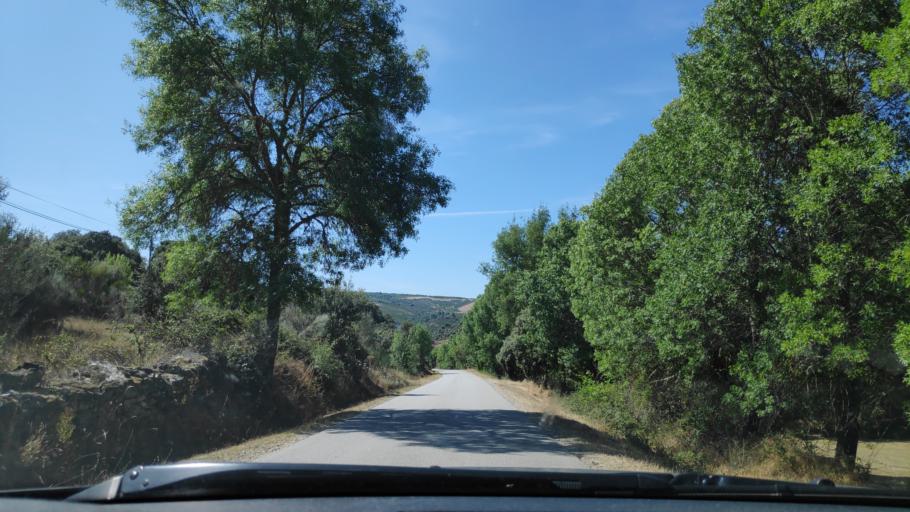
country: ES
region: Castille and Leon
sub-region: Provincia de Zamora
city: Trabazos
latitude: 41.7431
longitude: -6.5777
